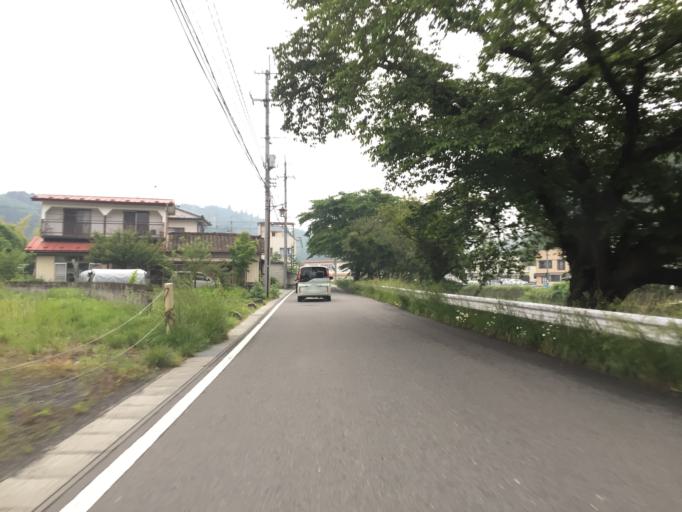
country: JP
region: Fukushima
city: Ishikawa
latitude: 37.1528
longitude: 140.4564
